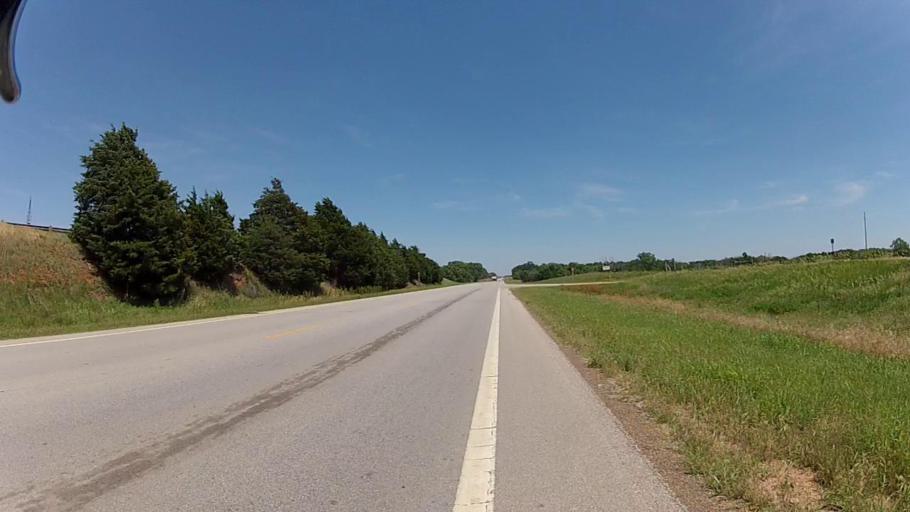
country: US
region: Kansas
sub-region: Harper County
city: Harper
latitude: 37.2390
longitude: -98.1667
